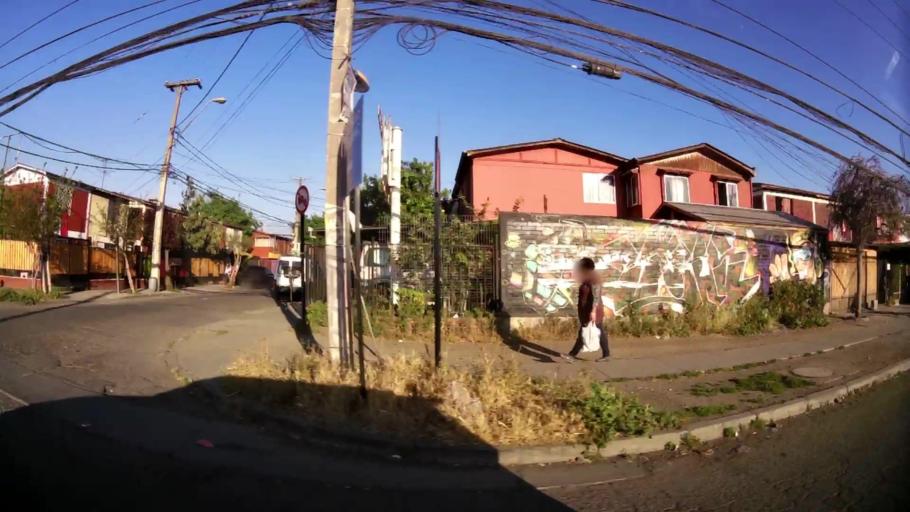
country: CL
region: Santiago Metropolitan
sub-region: Provincia de Santiago
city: Lo Prado
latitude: -33.4798
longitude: -70.7499
